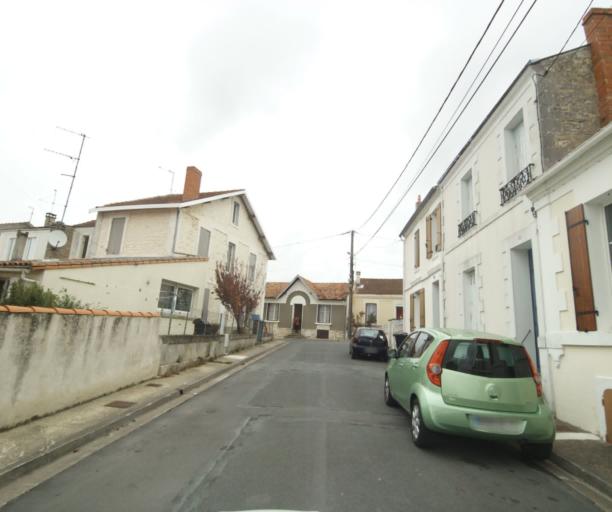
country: FR
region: Poitou-Charentes
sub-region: Departement de la Charente-Maritime
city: Saintes
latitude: 45.7463
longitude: -0.6113
